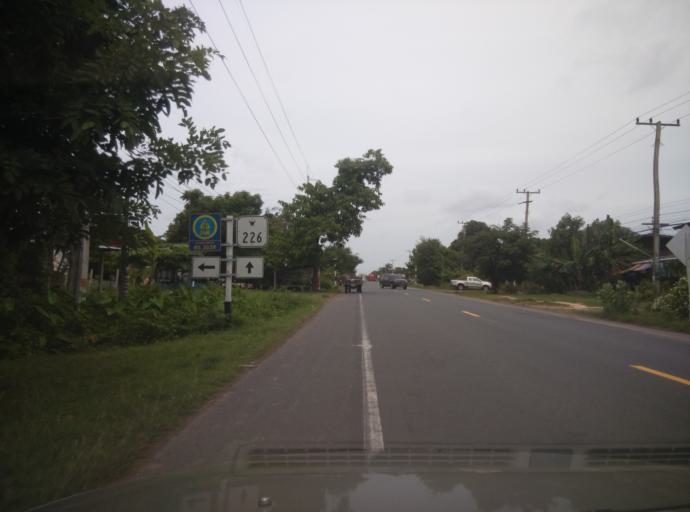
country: TH
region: Sisaket
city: Uthumphon Phisai
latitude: 15.0734
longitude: 104.0970
